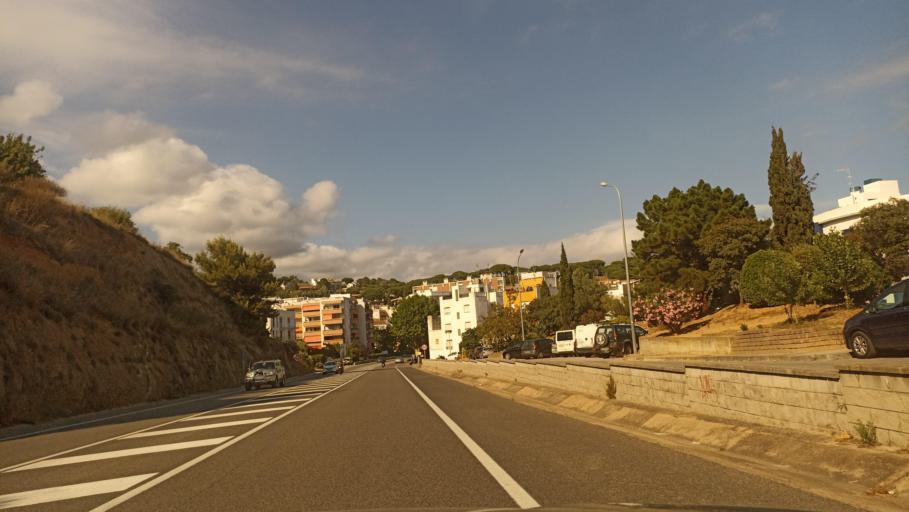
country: ES
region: Catalonia
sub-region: Provincia de Barcelona
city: Sant Pol de Mar
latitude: 41.6029
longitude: 2.6225
